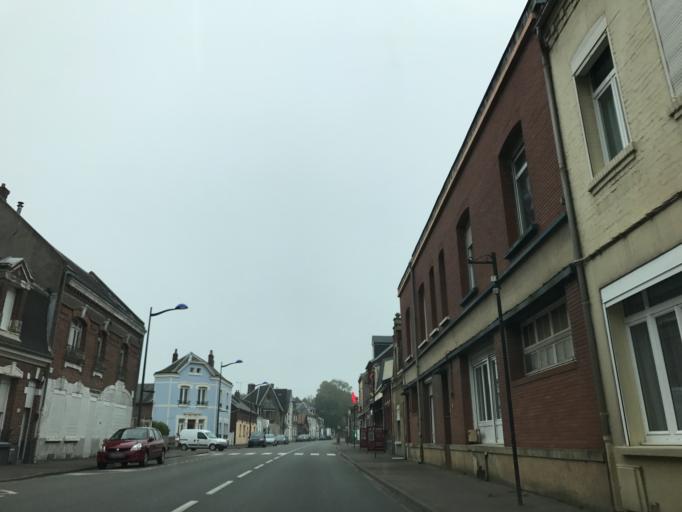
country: FR
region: Nord-Pas-de-Calais
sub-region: Departement du Pas-de-Calais
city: Bapaume
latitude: 50.0993
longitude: 2.8548
